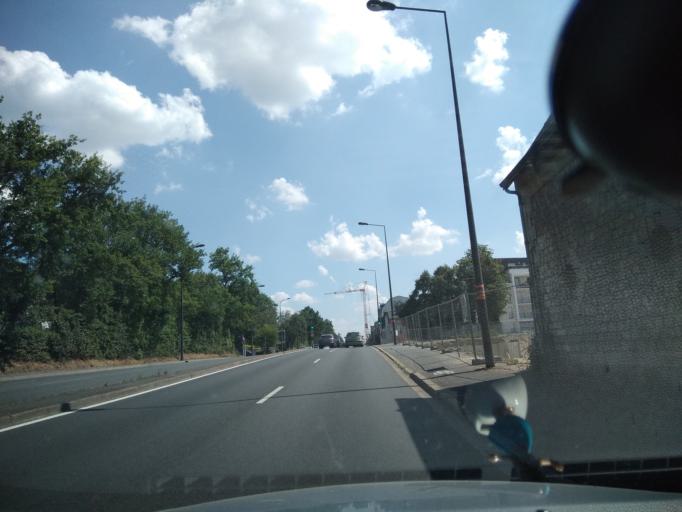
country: FR
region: Centre
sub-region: Departement d'Indre-et-Loire
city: Chambray-les-Tours
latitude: 47.3605
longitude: 0.6972
